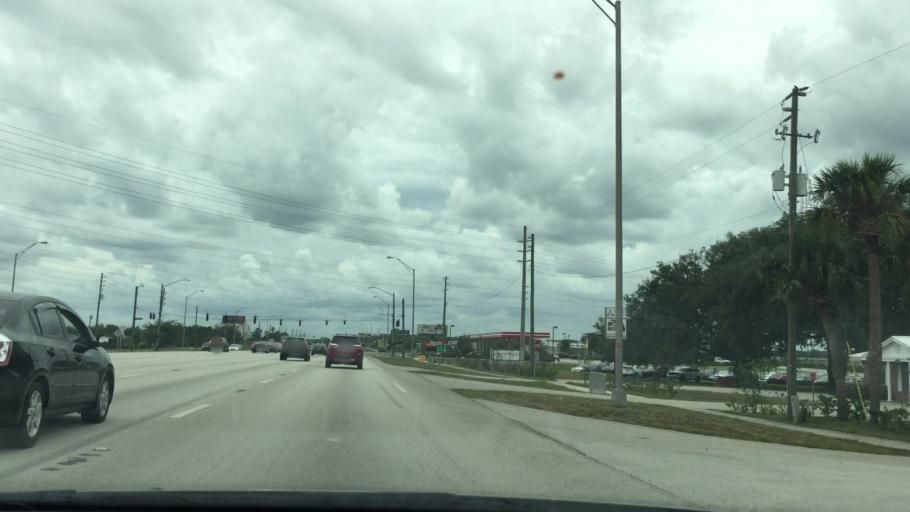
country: US
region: Florida
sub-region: Osceola County
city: Kissimmee
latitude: 28.3027
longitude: -81.3784
